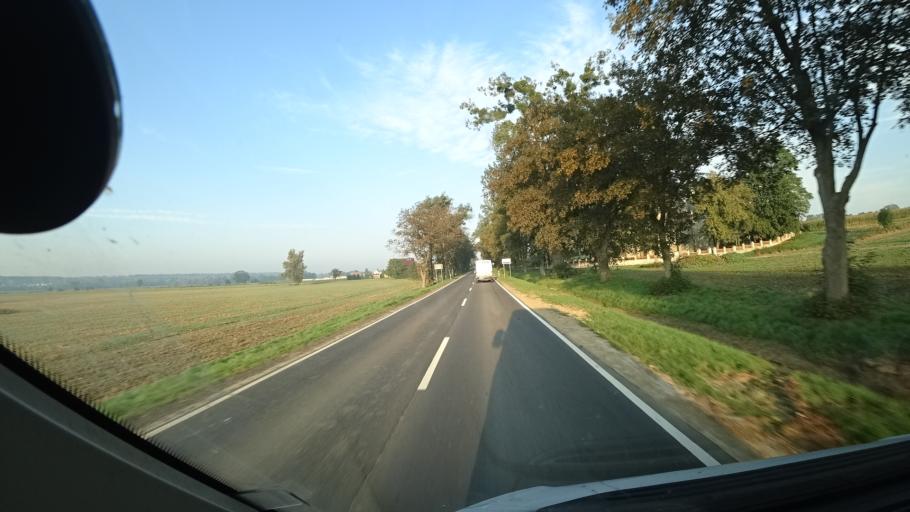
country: PL
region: Opole Voivodeship
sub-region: Powiat strzelecki
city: Ujazd
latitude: 50.3869
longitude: 18.3677
